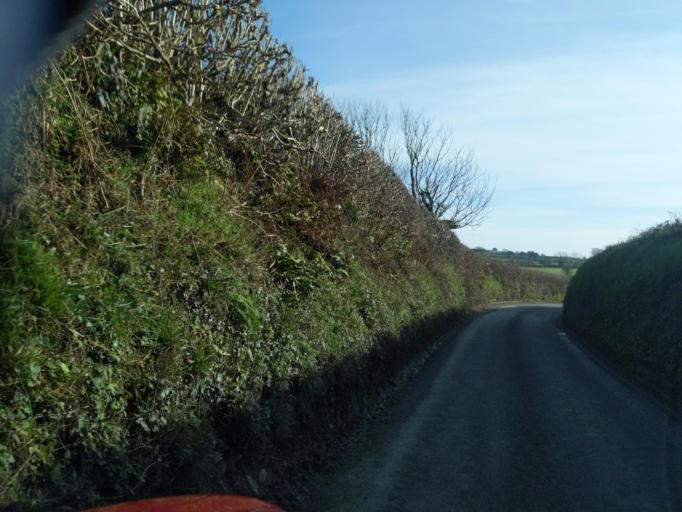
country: GB
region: England
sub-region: Devon
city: Kingsbridge
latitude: 50.3380
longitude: -3.7220
